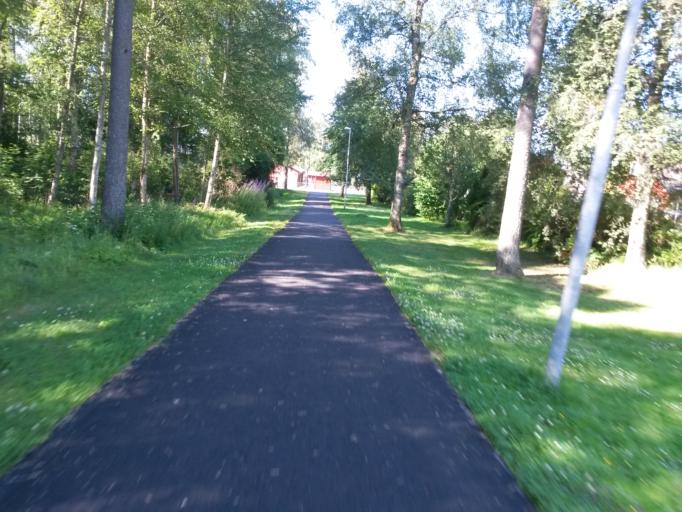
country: SE
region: Vaestra Goetaland
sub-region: Vargarda Kommun
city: Vargarda
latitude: 58.0375
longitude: 12.8199
